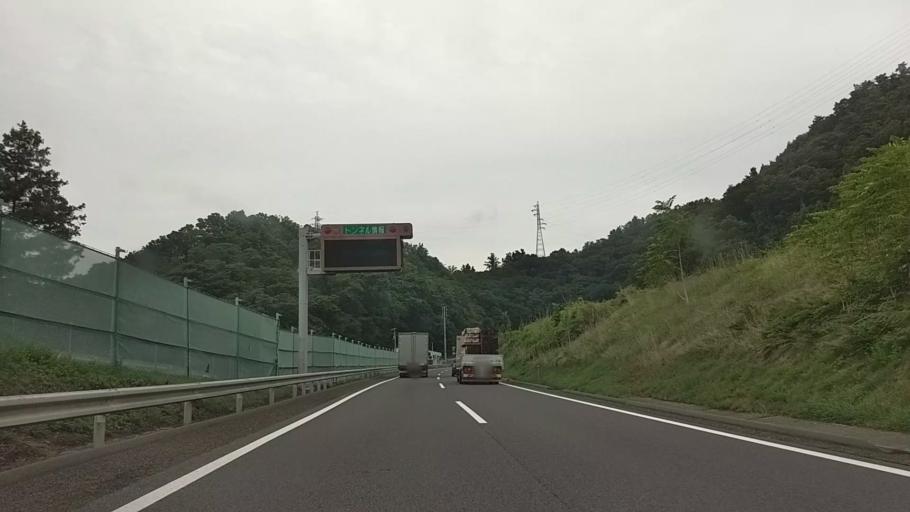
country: JP
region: Nagano
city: Nagano-shi
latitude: 36.5444
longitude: 138.0980
